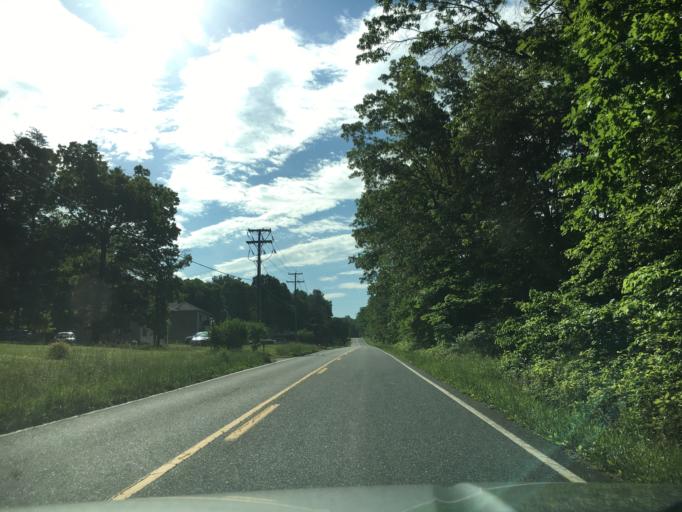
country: US
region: Virginia
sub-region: Campbell County
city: Rustburg
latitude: 37.3275
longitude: -79.1547
